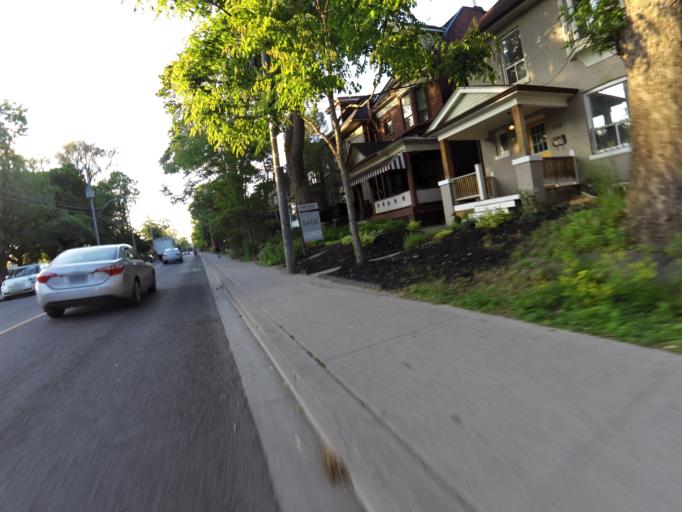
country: CA
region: Ontario
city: Toronto
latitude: 43.6528
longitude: -79.4407
